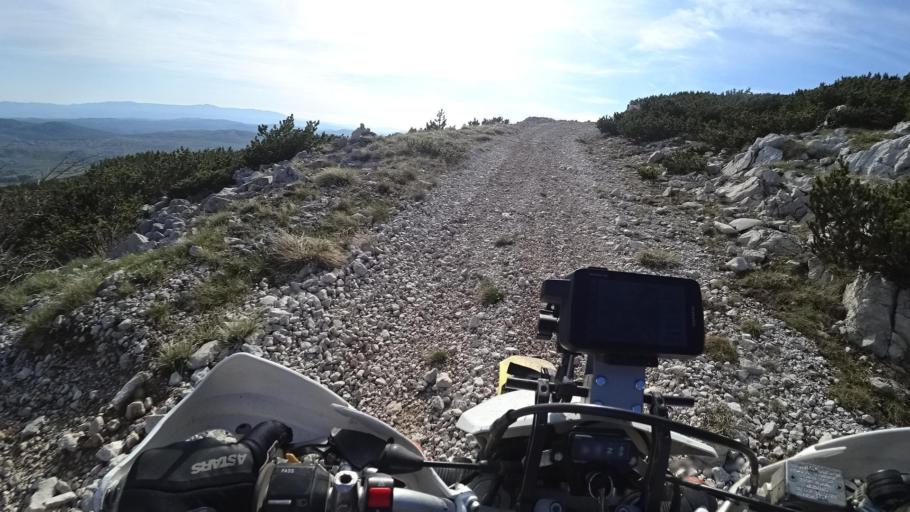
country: BA
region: Federation of Bosnia and Herzegovina
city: Kocerin
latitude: 43.5935
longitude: 17.5407
